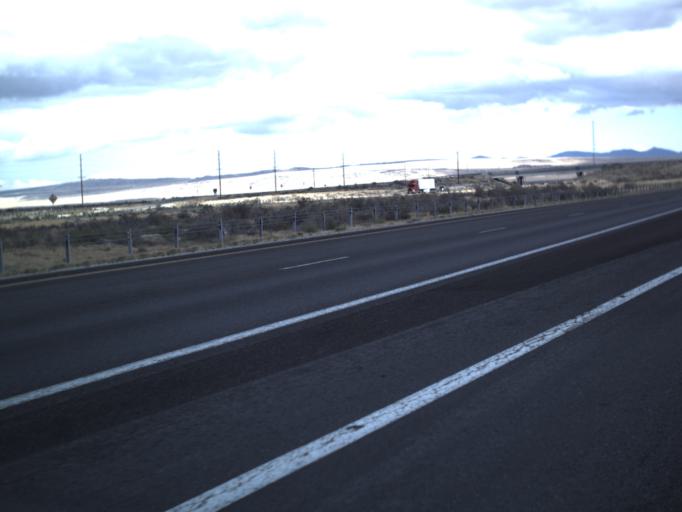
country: US
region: Utah
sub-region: Tooele County
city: Grantsville
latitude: 40.7296
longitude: -113.1204
